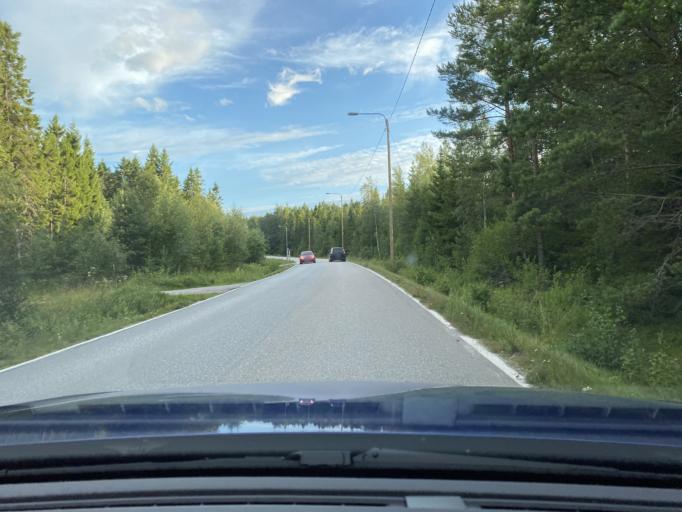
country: FI
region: Ostrobothnia
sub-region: Vaasa
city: Korsnaes
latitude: 62.9548
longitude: 21.1787
